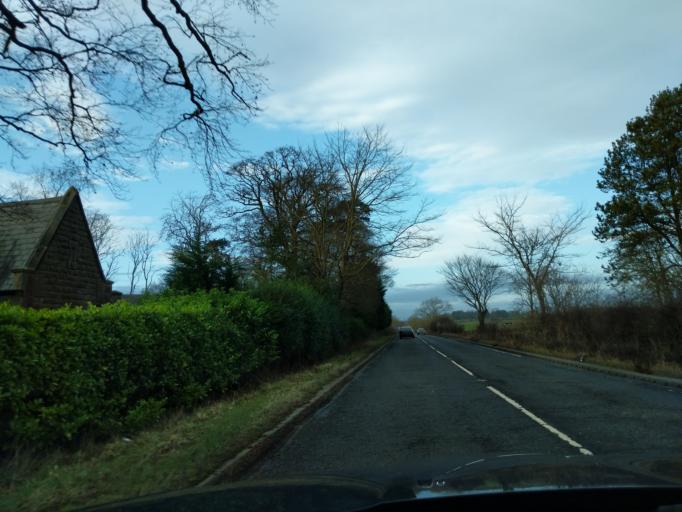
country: GB
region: England
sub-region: Northumberland
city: Darras Hall
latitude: 55.0622
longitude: -1.7756
